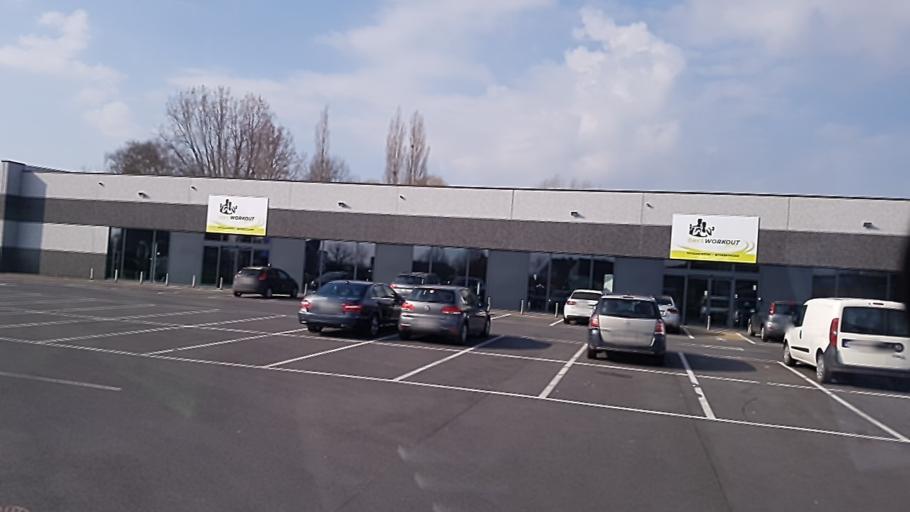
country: BE
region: Flanders
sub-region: Provincie West-Vlaanderen
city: Ieper
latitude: 50.8398
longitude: 2.8868
